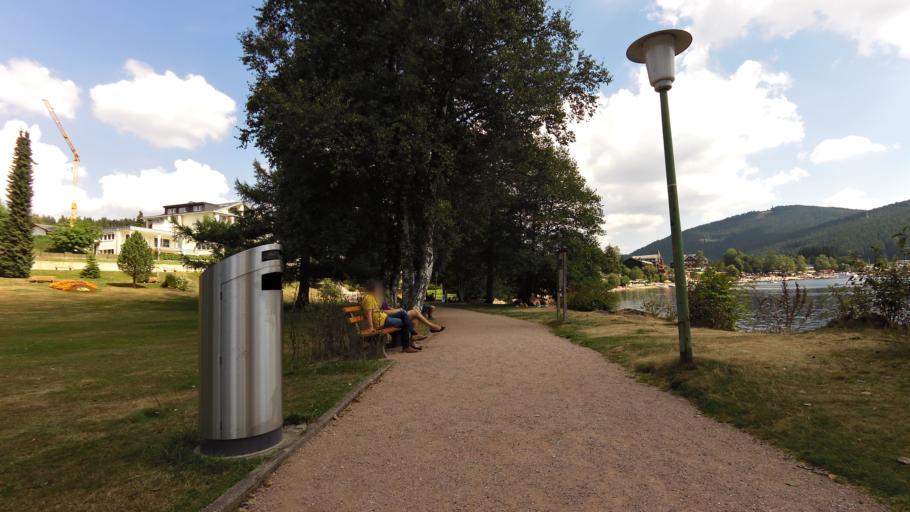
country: DE
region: Baden-Wuerttemberg
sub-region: Freiburg Region
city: Hinterzarten
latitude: 47.8991
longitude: 8.1465
